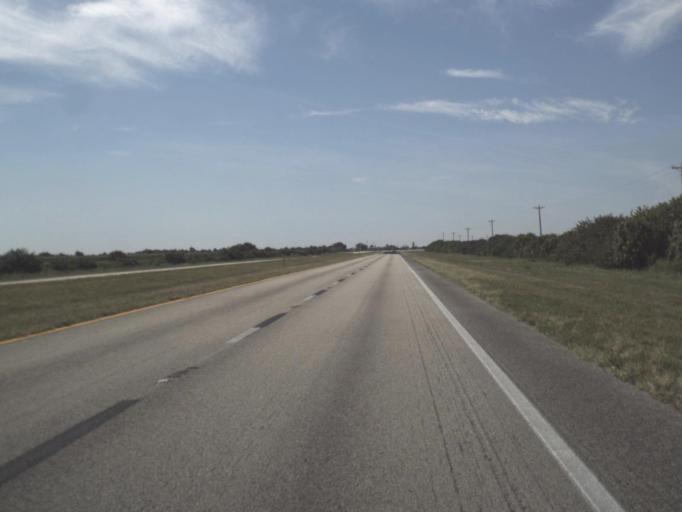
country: US
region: Florida
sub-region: Glades County
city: Moore Haven
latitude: 26.8338
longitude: -81.1795
